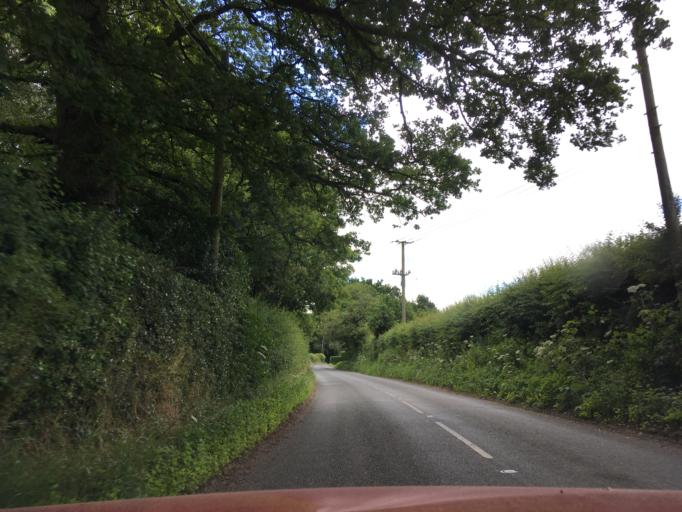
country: GB
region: England
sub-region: West Berkshire
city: Welford
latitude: 51.4486
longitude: -1.4029
